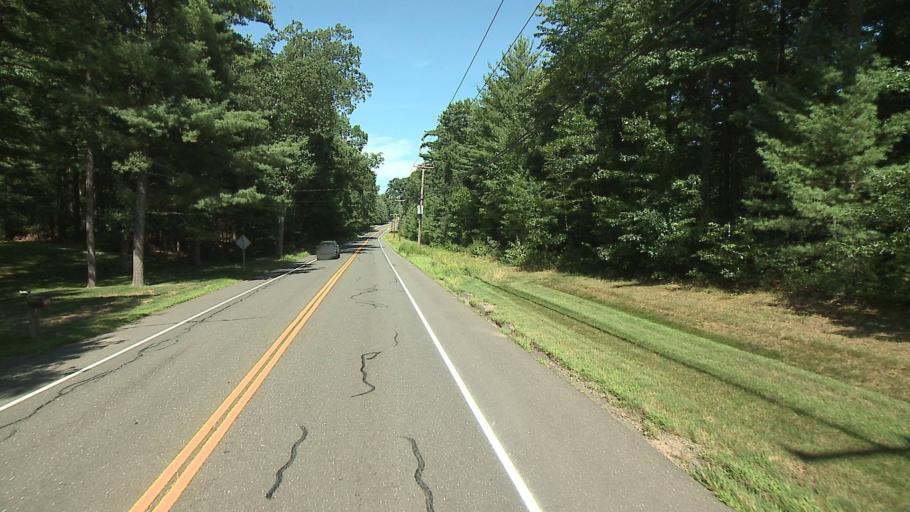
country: US
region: Connecticut
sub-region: Hartford County
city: Weatogue
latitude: 41.8628
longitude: -72.8259
